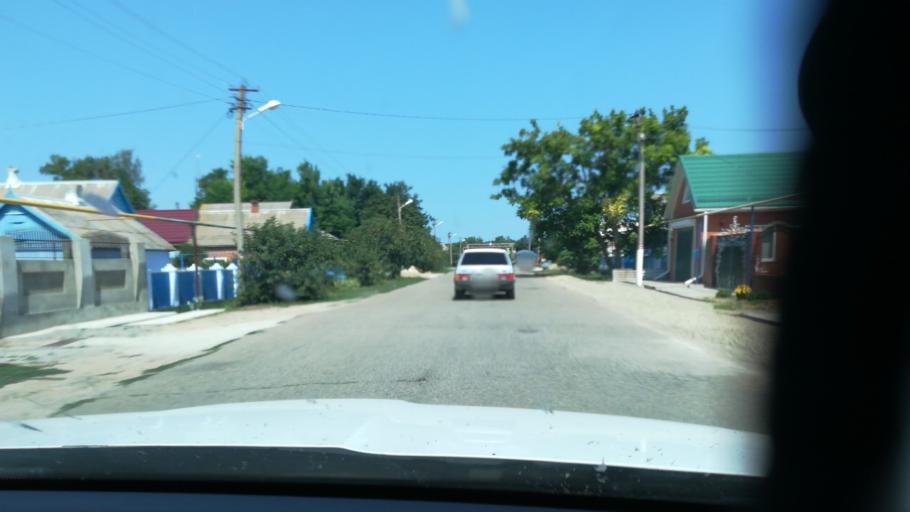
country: RU
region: Krasnodarskiy
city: Starotitarovskaya
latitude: 45.2150
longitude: 37.1430
